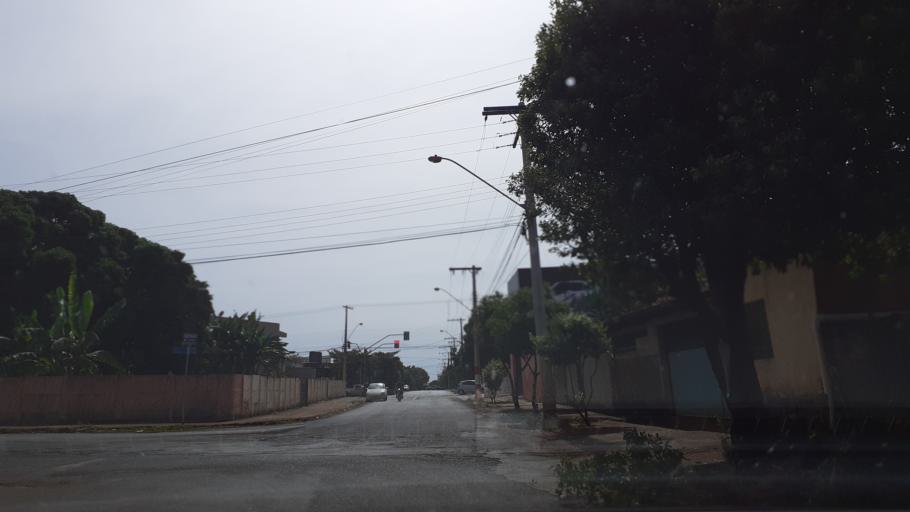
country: BR
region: Goias
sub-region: Itumbiara
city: Itumbiara
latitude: -18.4186
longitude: -49.2323
